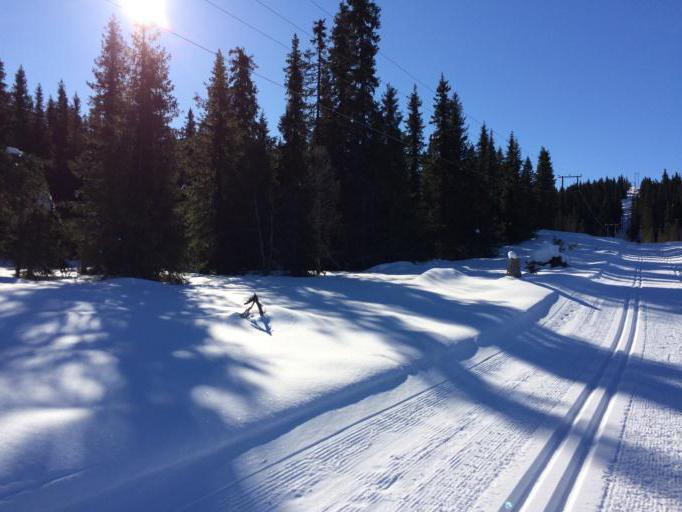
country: NO
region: Oppland
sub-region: Gausdal
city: Segalstad bru
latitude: 61.3179
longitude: 10.0783
